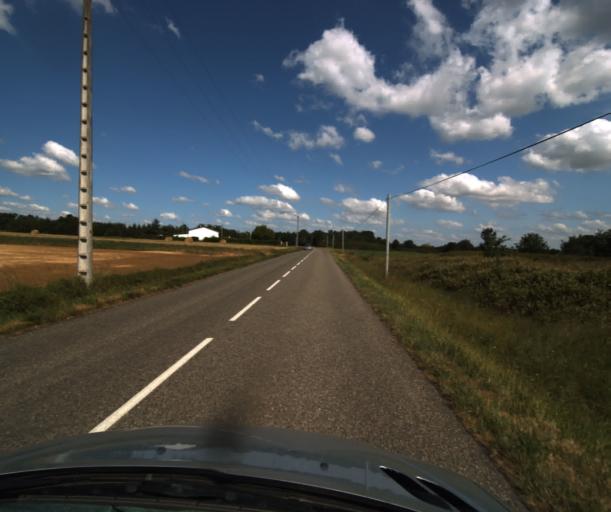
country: FR
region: Midi-Pyrenees
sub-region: Departement du Tarn-et-Garonne
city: Campsas
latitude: 43.9062
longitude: 1.2910
